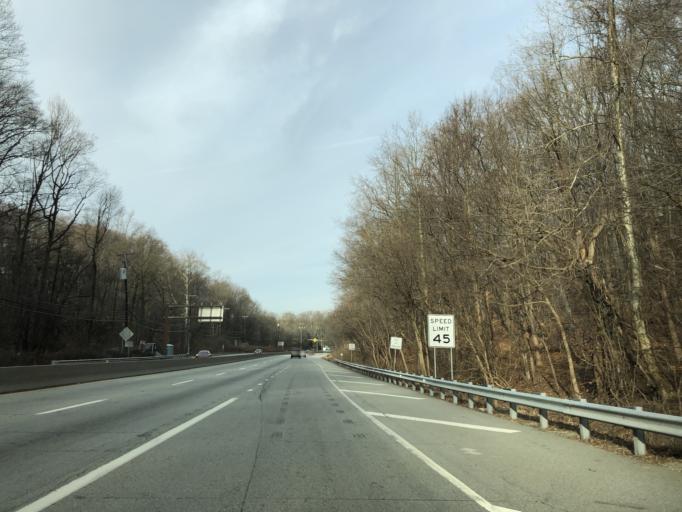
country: US
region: Pennsylvania
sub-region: Chester County
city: Exton
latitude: 40.0158
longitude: -75.6190
